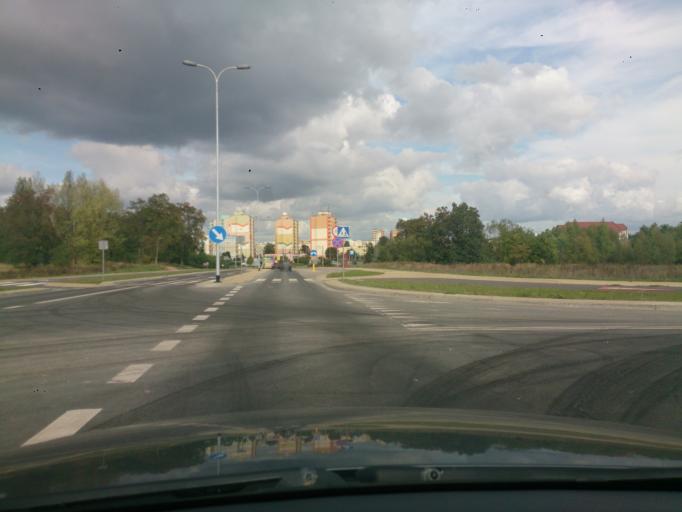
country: PL
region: Kujawsko-Pomorskie
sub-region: Grudziadz
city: Grudziadz
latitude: 53.4474
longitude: 18.7153
